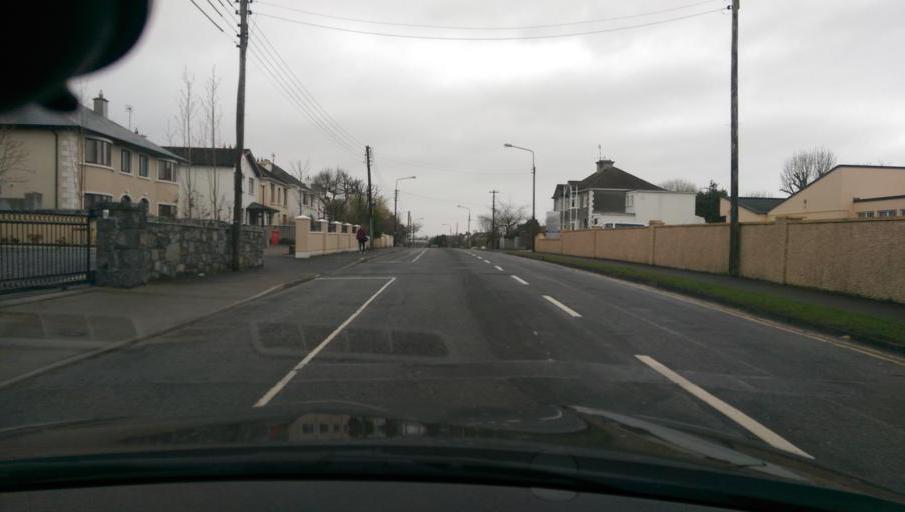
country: IE
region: Connaught
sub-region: County Galway
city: Gaillimh
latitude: 53.2844
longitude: -9.0671
